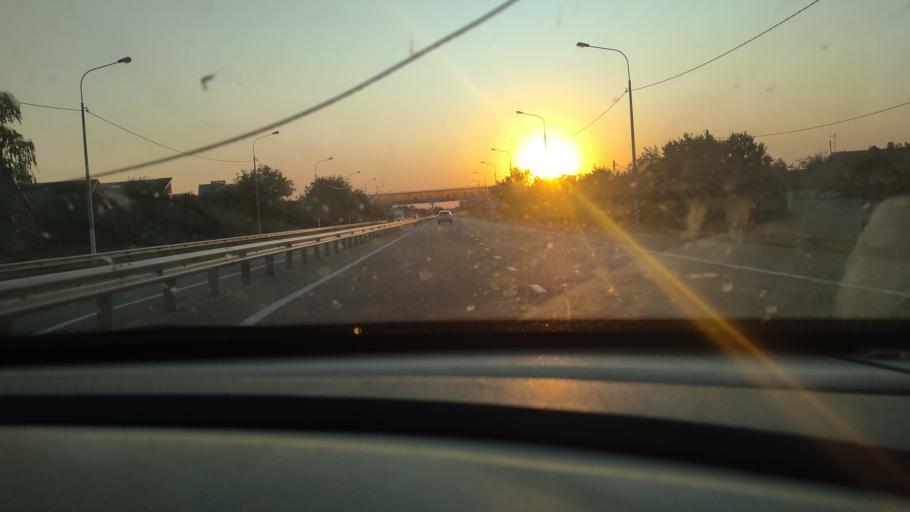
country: RU
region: Krasnodarskiy
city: Timashevsk
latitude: 45.6010
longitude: 38.9535
